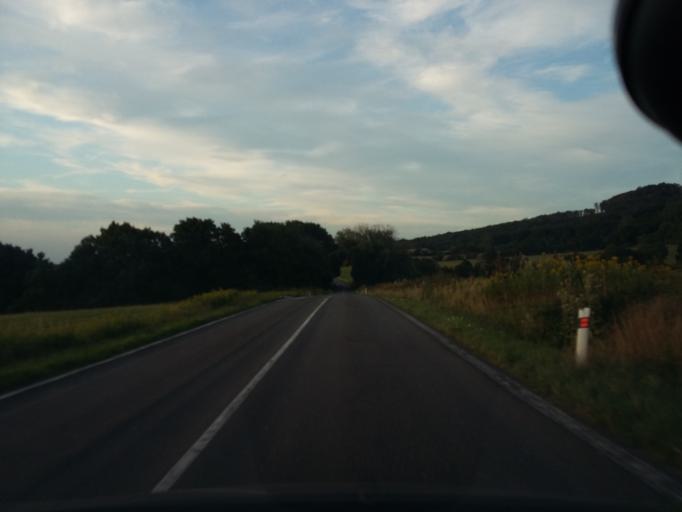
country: SK
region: Bratislavsky
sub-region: Okres Malacky
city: Malacky
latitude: 48.3819
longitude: 17.1522
